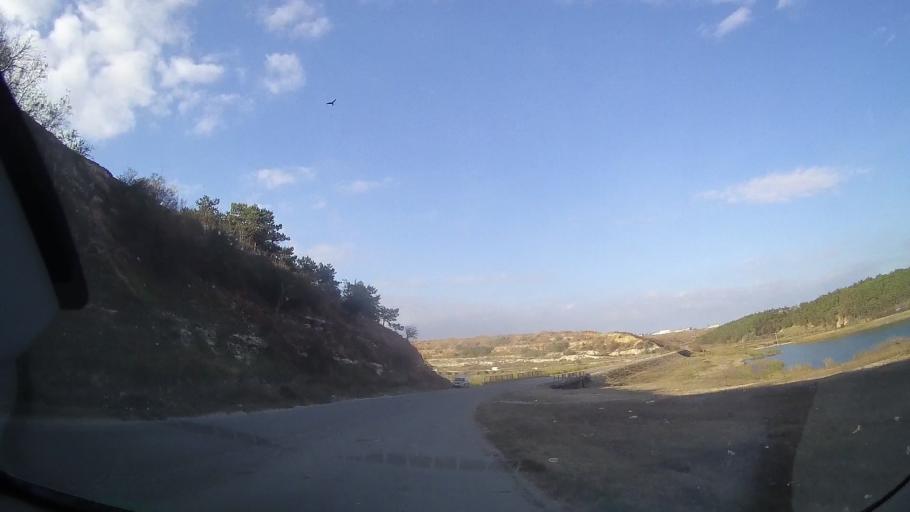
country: RO
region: Constanta
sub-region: Comuna Limanu
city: Limanu
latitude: 43.8116
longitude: 28.5171
